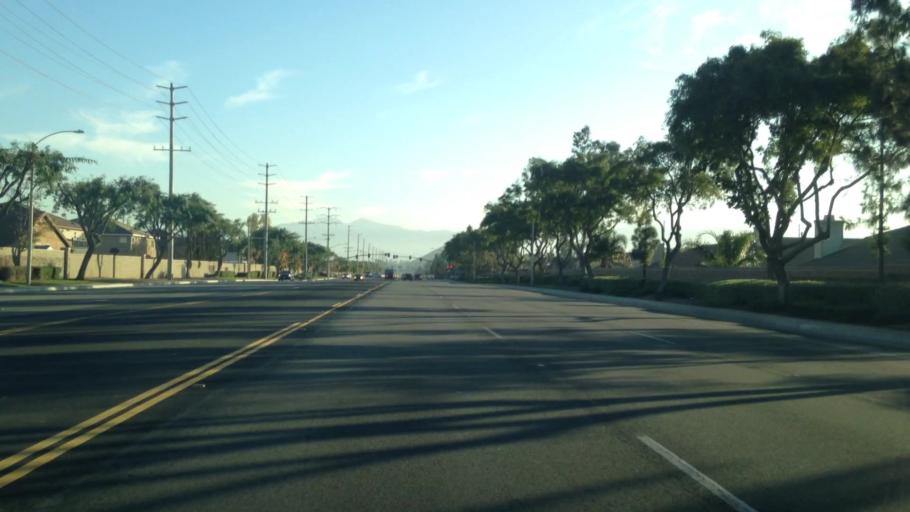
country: US
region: California
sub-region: Riverside County
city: Norco
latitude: 33.9674
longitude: -117.5584
